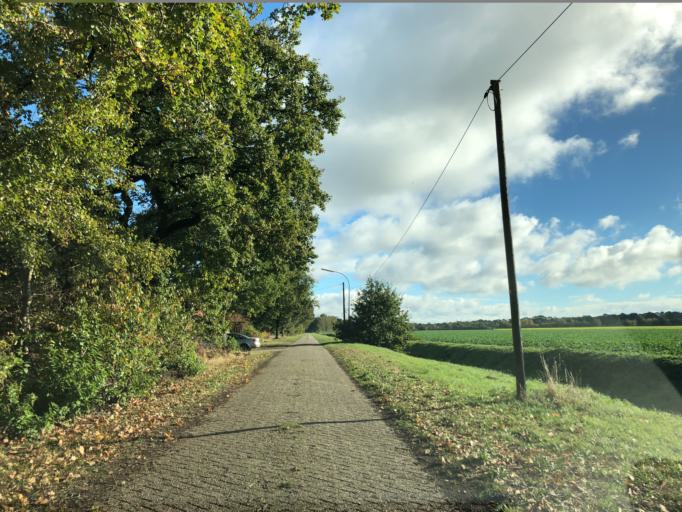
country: DE
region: Lower Saxony
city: Lehe
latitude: 53.0358
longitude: 7.3589
